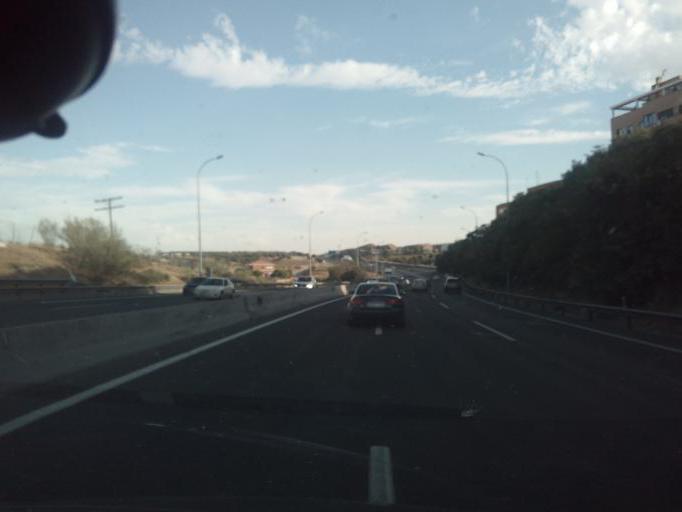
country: ES
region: Madrid
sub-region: Provincia de Madrid
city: Valdemoro
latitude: 40.1911
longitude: -3.6718
